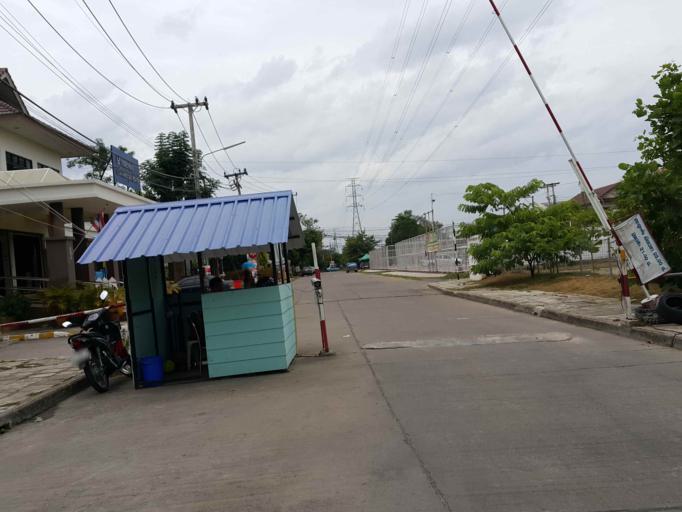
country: TH
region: Chiang Mai
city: Chiang Mai
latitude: 18.7597
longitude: 99.0091
